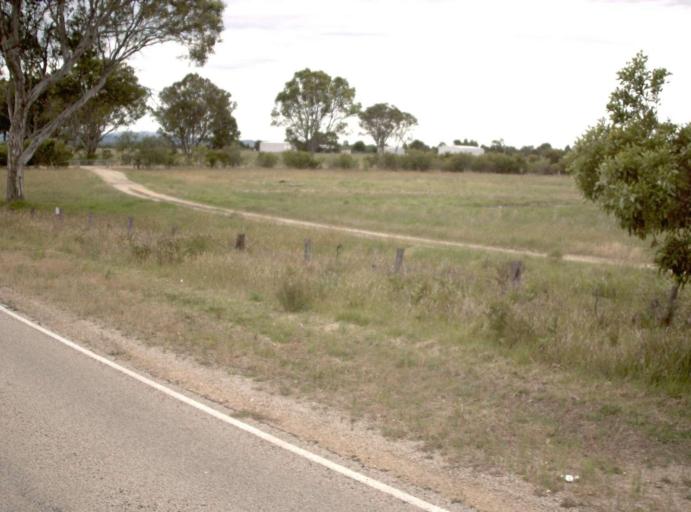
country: AU
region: Victoria
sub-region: East Gippsland
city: Bairnsdale
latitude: -37.8795
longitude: 147.5592
